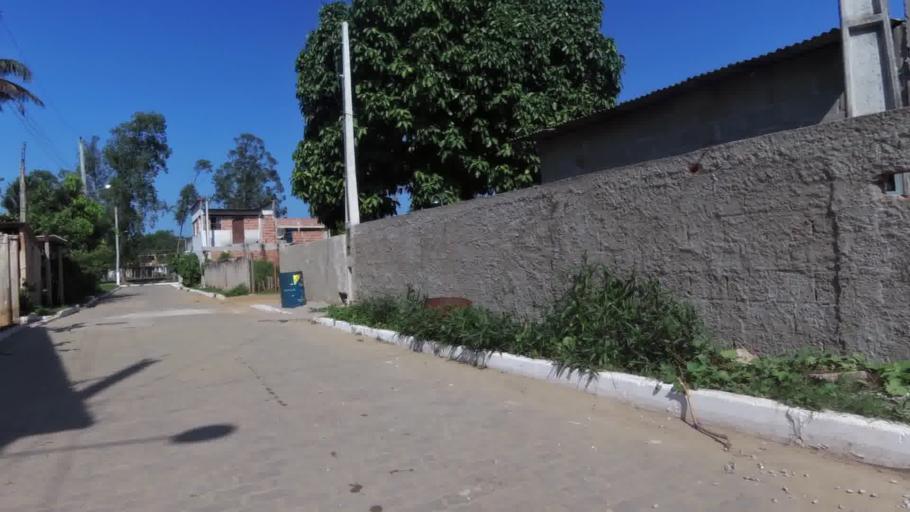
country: BR
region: Espirito Santo
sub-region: Piuma
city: Piuma
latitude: -20.8091
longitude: -40.7383
